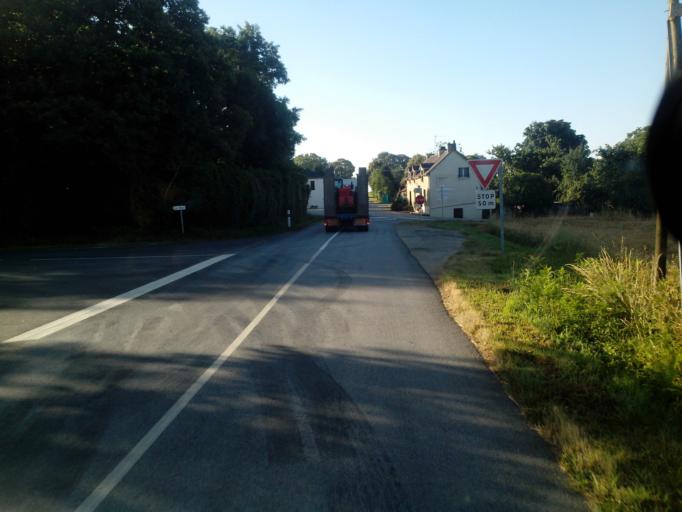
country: FR
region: Brittany
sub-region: Departement du Morbihan
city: Guilliers
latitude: 48.0816
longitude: -2.4421
